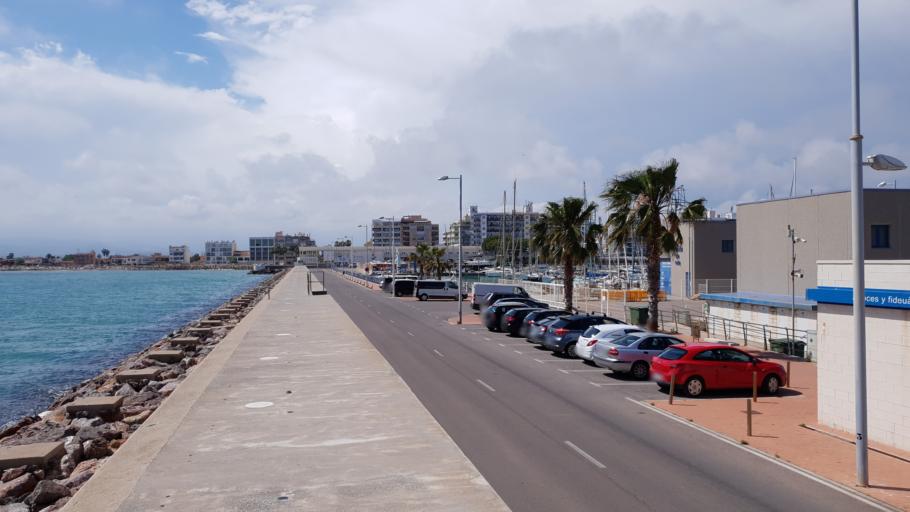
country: ES
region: Valencia
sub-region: Provincia de Castello
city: Burriana
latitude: 39.8602
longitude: -0.0730
